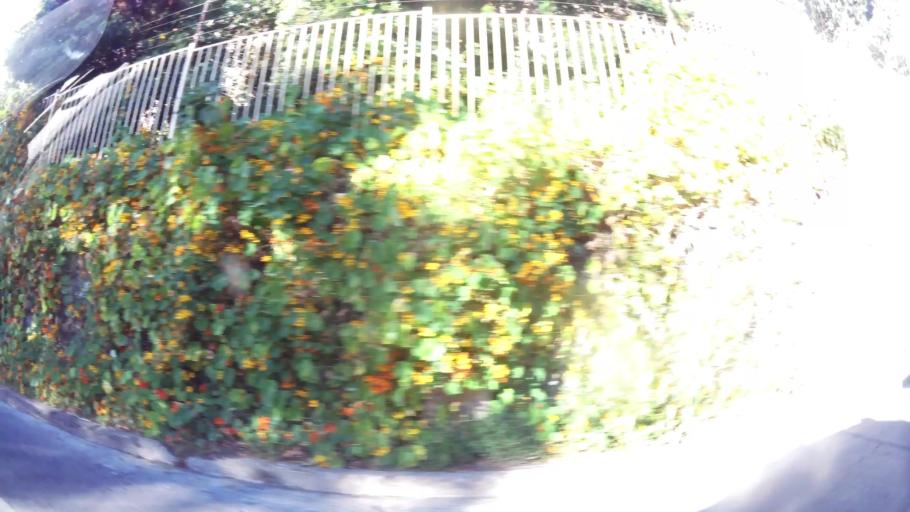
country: CL
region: Valparaiso
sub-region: Provincia de Valparaiso
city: Vina del Mar
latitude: -33.0299
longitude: -71.5835
